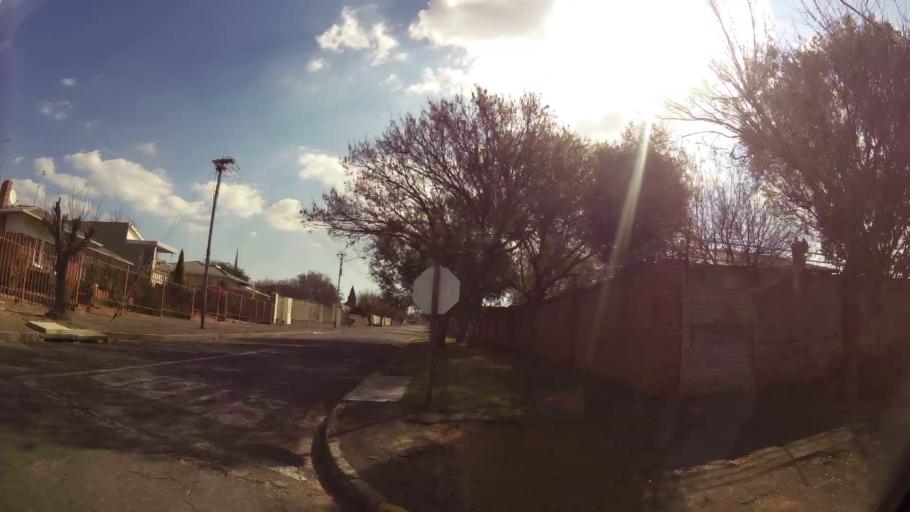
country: ZA
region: Gauteng
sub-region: Ekurhuleni Metropolitan Municipality
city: Germiston
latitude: -26.1822
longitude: 28.1847
